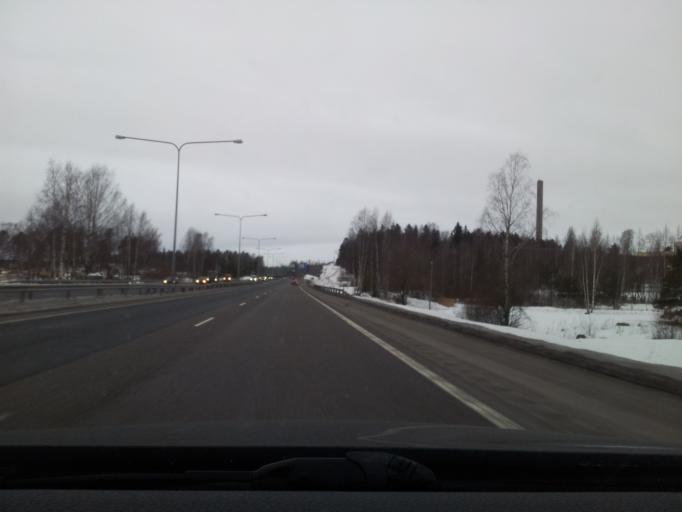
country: FI
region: Uusimaa
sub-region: Helsinki
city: Espoo
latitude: 60.1567
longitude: 24.6369
